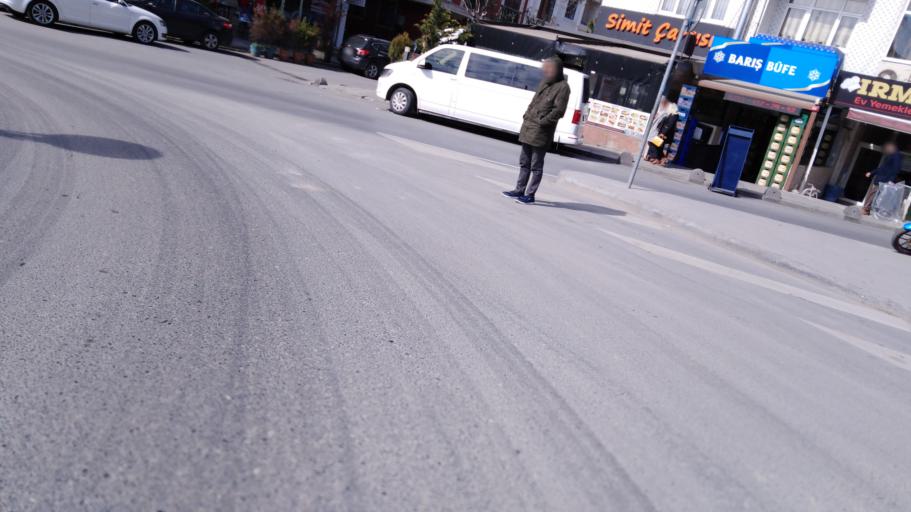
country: TR
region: Istanbul
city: Esenler
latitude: 41.0488
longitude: 28.8989
